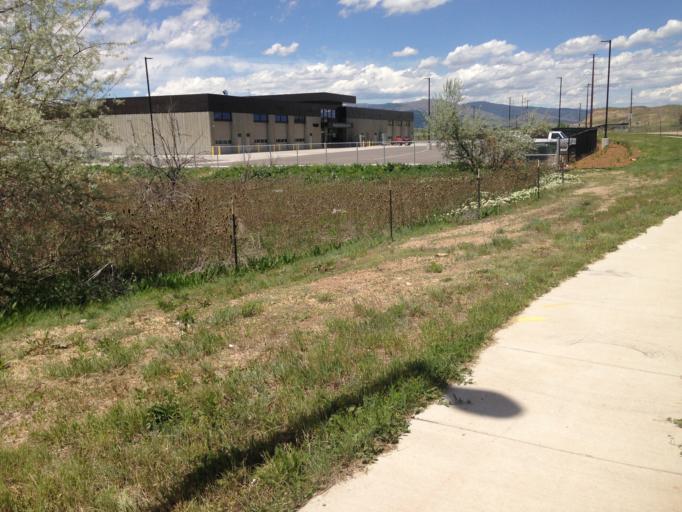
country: US
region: Colorado
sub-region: Boulder County
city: Gunbarrel
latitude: 40.0203
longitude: -105.2068
